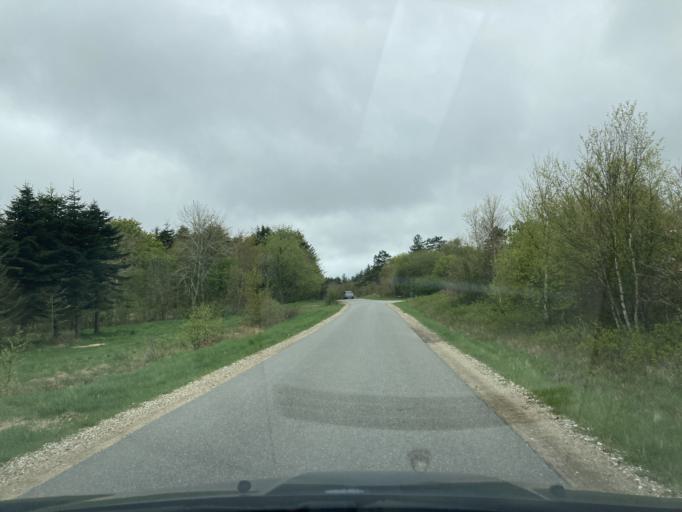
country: DK
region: North Denmark
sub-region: Thisted Kommune
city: Hurup
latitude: 56.8158
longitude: 8.3033
